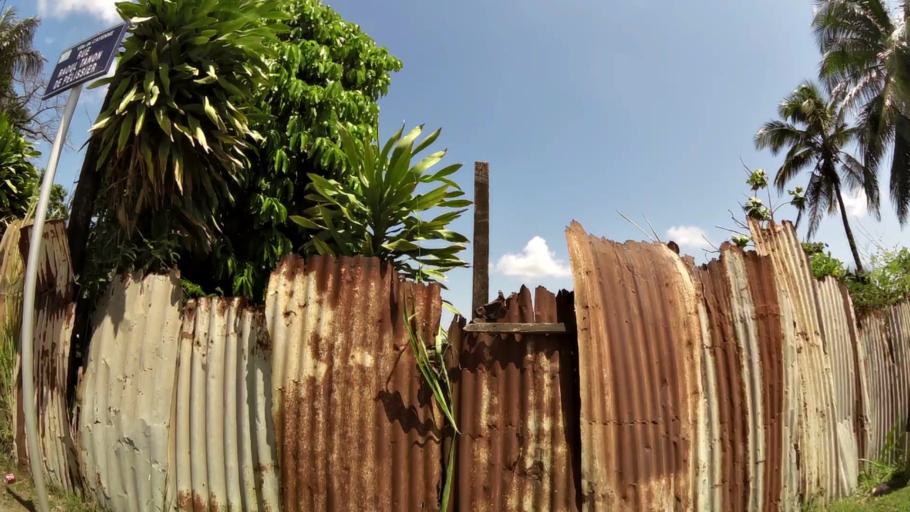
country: GF
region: Guyane
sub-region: Guyane
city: Cayenne
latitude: 4.9067
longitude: -52.3249
